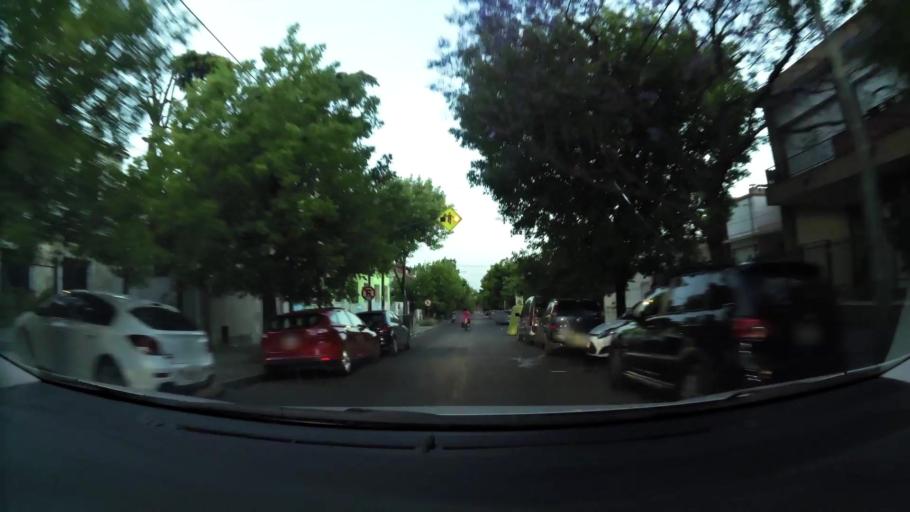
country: AR
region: Buenos Aires F.D.
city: Villa Lugano
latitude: -34.6830
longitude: -58.4781
